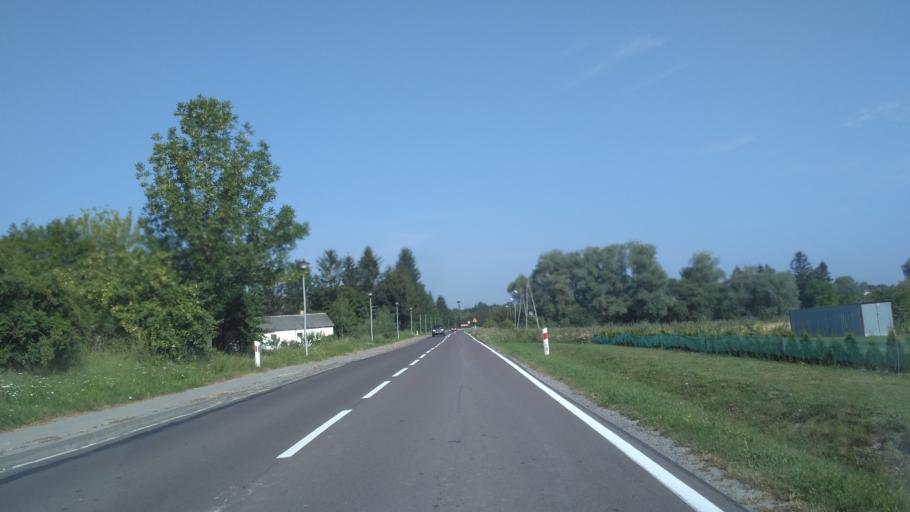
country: PL
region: Lublin Voivodeship
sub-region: Powiat chelmski
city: Rejowiec Fabryczny
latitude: 51.1880
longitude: 23.1663
